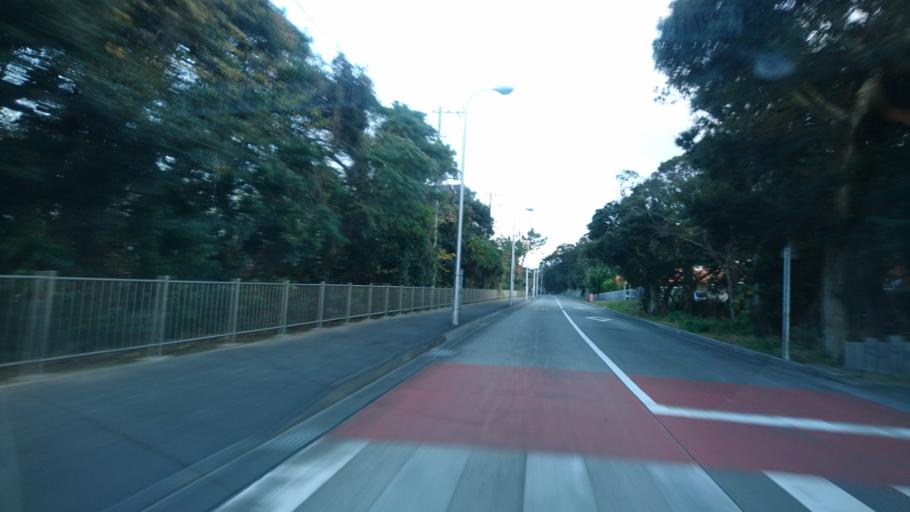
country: JP
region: Shizuoka
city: Shimoda
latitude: 34.3691
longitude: 139.2570
